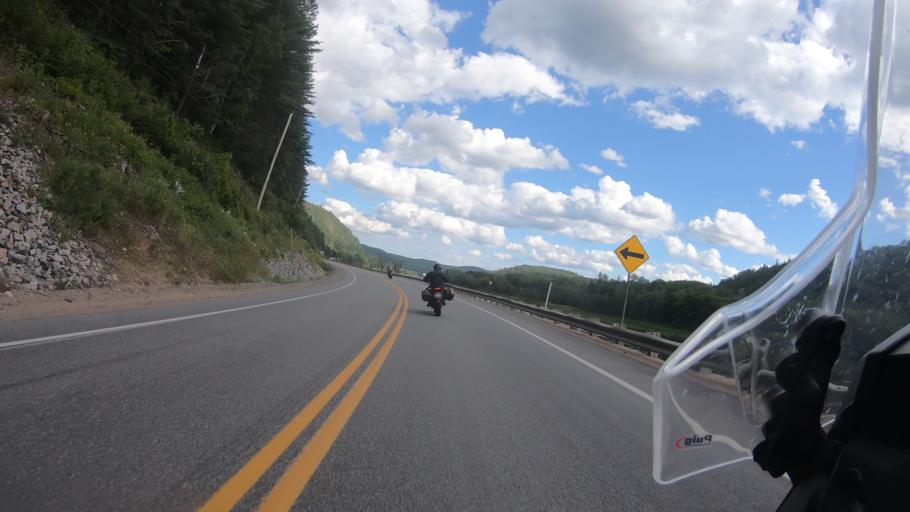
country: CA
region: Quebec
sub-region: Mauricie
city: Saint-Tite
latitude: 46.9986
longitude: -72.9232
